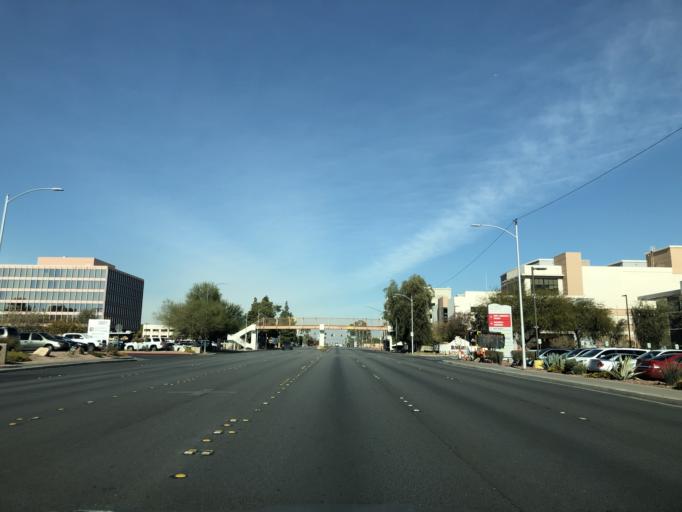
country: US
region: Nevada
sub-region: Clark County
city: Winchester
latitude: 36.1310
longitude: -115.1369
